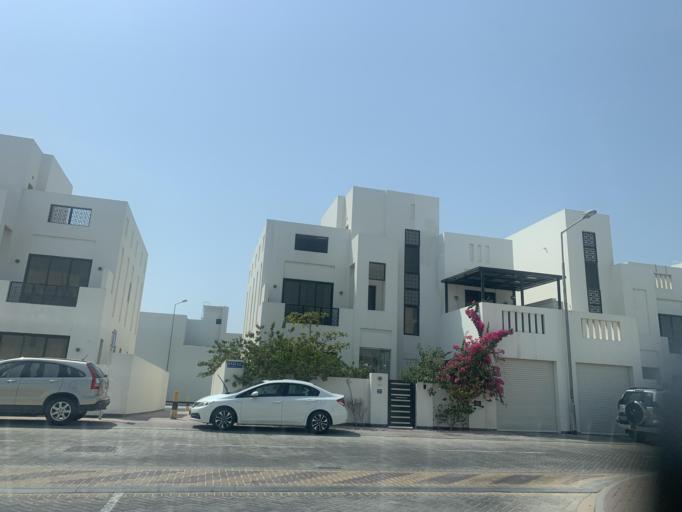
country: BH
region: Muharraq
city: Al Muharraq
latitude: 26.3012
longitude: 50.6329
